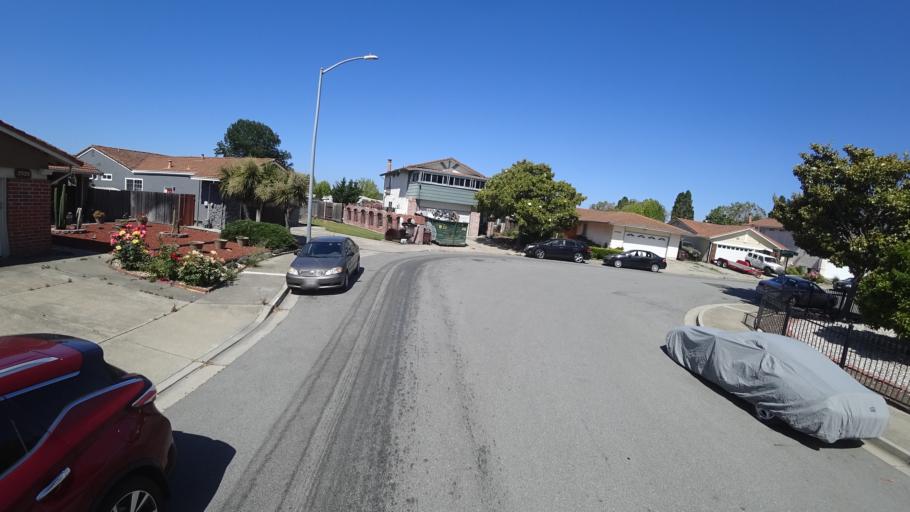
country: US
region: California
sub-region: Alameda County
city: Hayward
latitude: 37.6230
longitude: -122.0960
